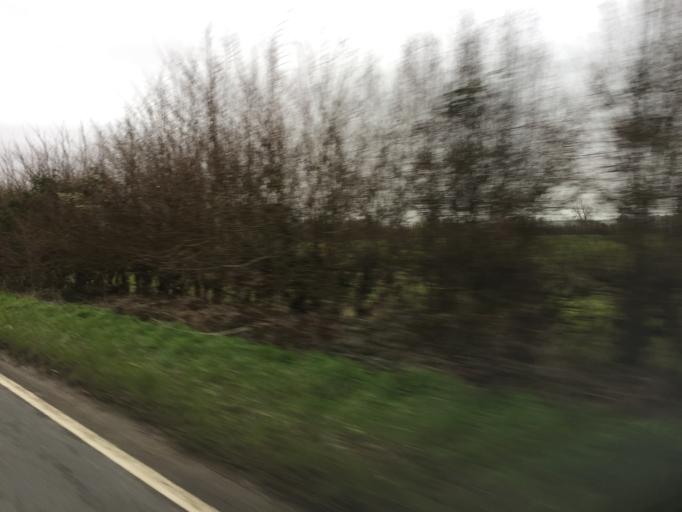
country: GB
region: England
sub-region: Oxfordshire
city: Stanford in the Vale
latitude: 51.6084
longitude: -1.4794
